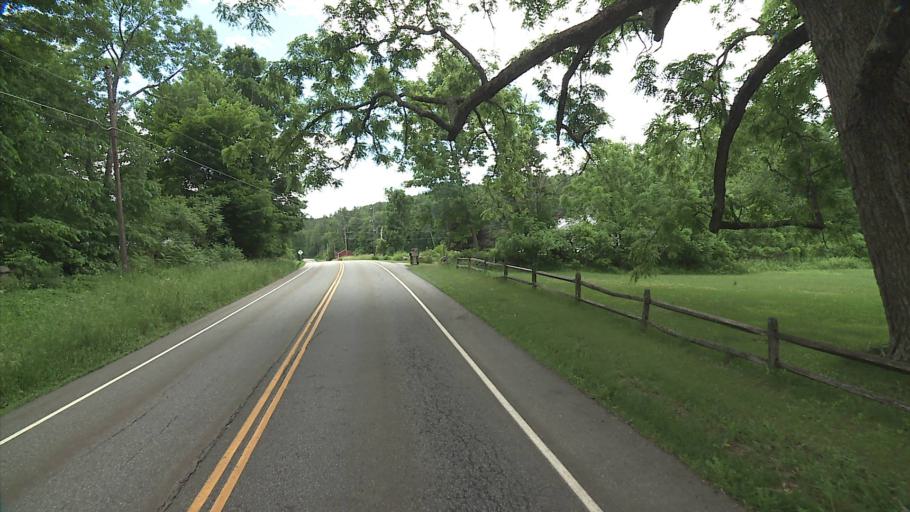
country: US
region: Connecticut
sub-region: Litchfield County
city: Winchester Center
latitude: 41.8994
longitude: -73.2674
